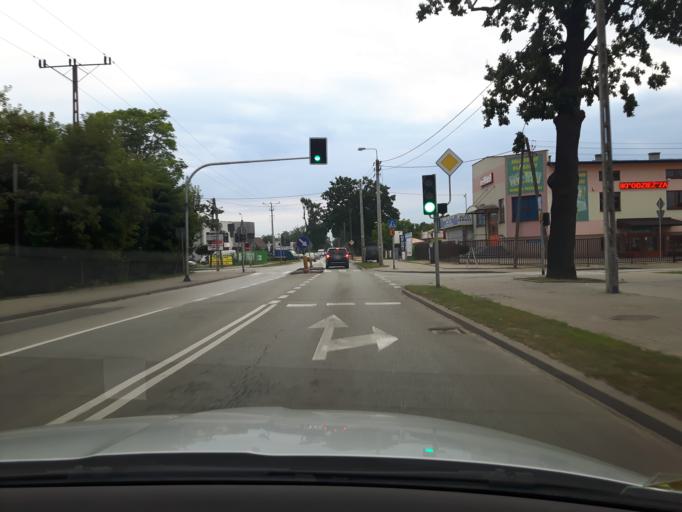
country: PL
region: Masovian Voivodeship
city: Zielonka
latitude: 52.3026
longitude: 21.1587
